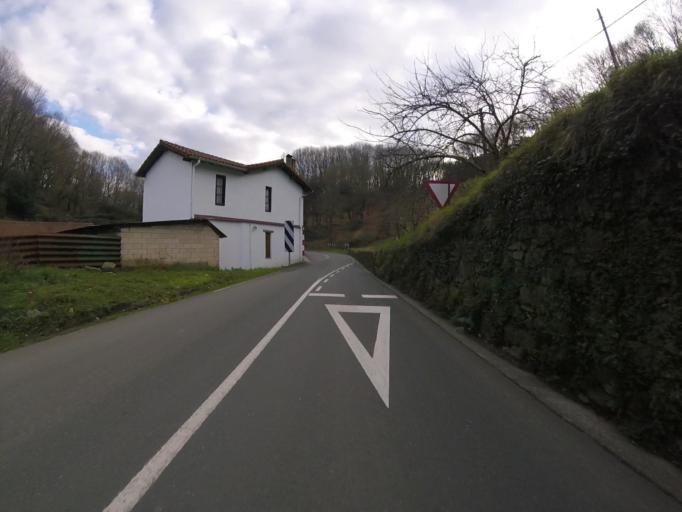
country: ES
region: Basque Country
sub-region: Provincia de Guipuzcoa
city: Irun
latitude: 43.3160
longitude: -1.8190
